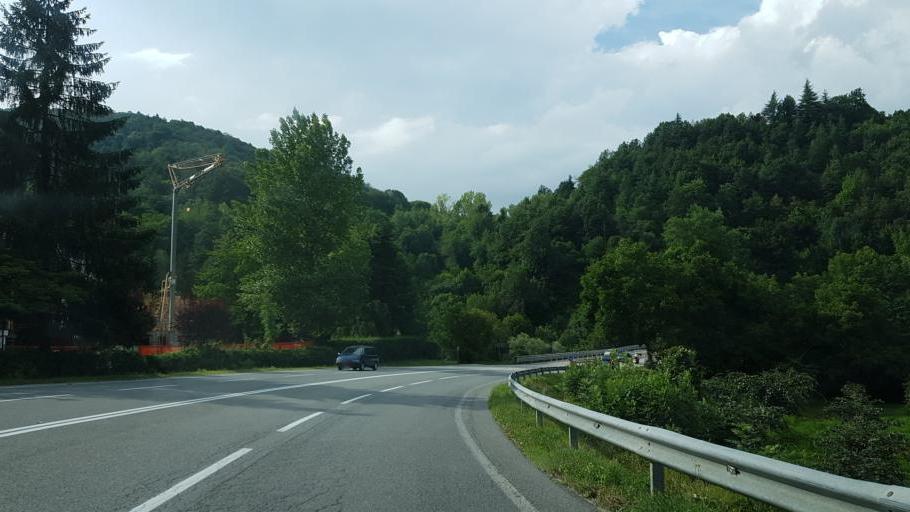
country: IT
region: Piedmont
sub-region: Provincia di Cuneo
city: Vignolo
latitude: 44.3455
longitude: 7.4741
